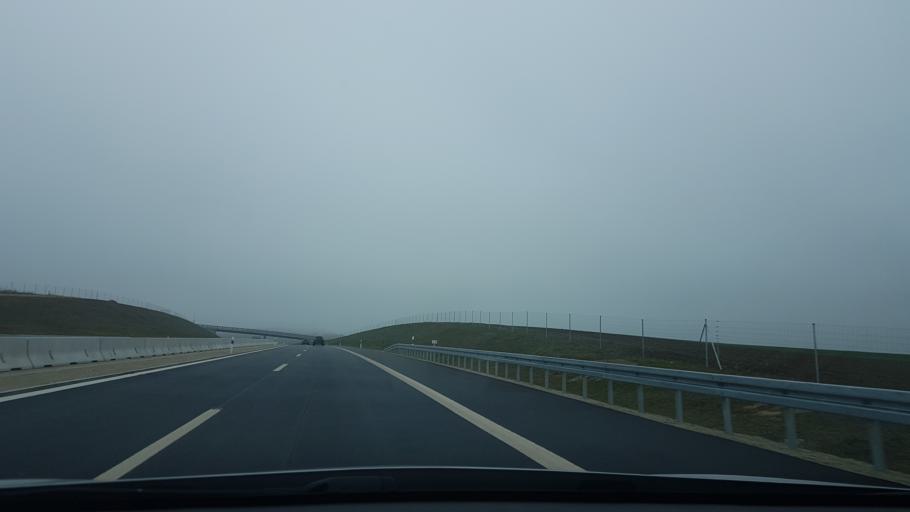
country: DE
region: Bavaria
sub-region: Lower Bavaria
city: Essenbach
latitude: 48.6383
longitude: 12.2036
